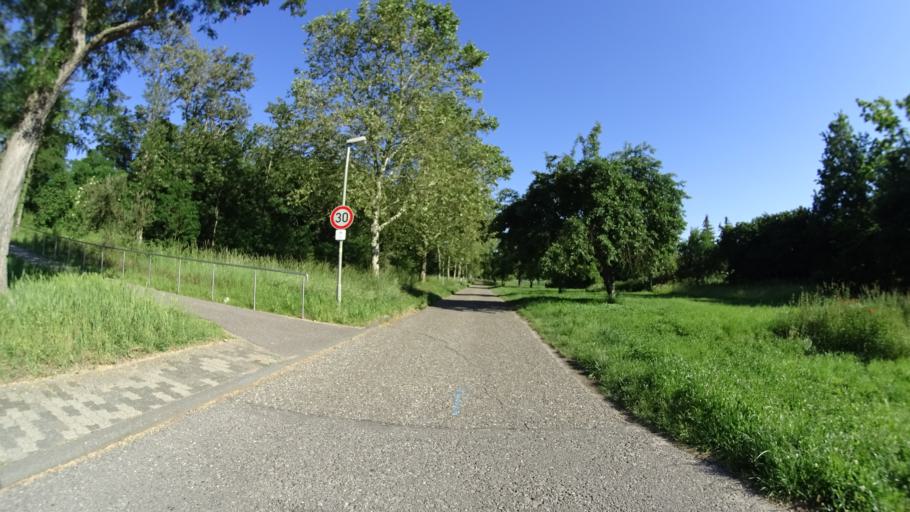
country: DE
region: Baden-Wuerttemberg
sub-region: Karlsruhe Region
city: Eggenstein-Leopoldshafen
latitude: 49.0963
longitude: 8.3947
